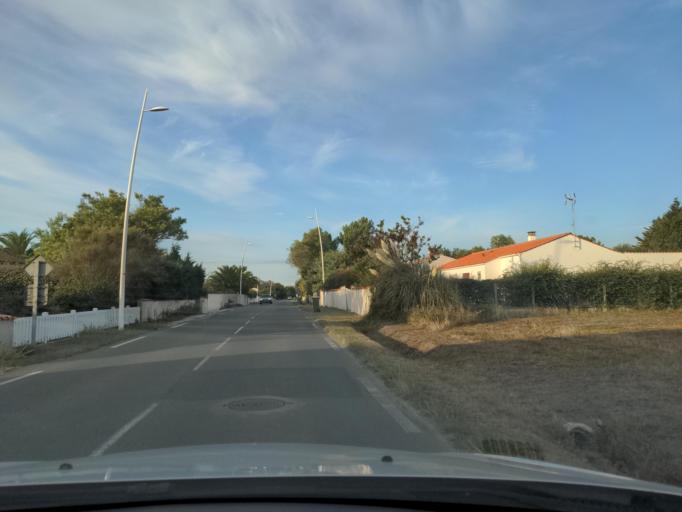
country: FR
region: Poitou-Charentes
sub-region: Departement de la Charente-Maritime
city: Saint-Trojan-les-Bains
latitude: 45.8841
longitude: -1.2111
